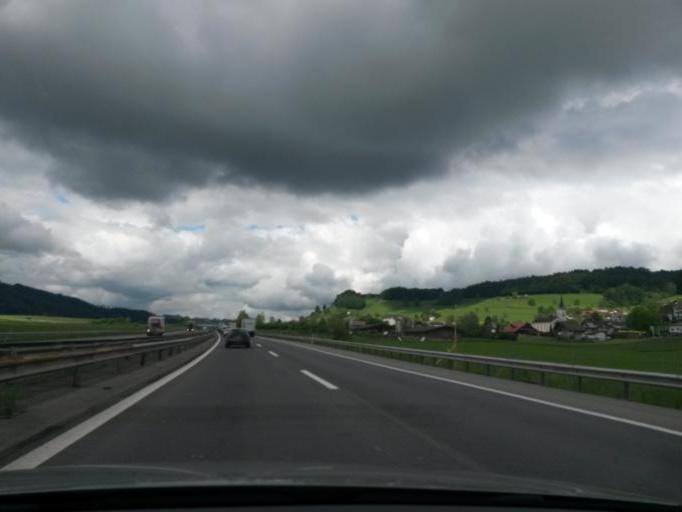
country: CH
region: Lucerne
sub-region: Willisau District
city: Wauwil
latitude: 47.2082
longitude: 8.0250
